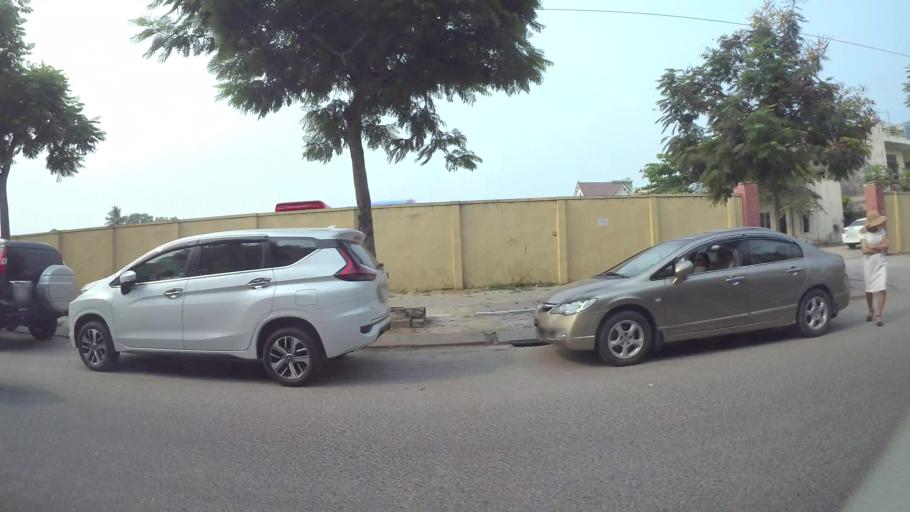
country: VN
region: Da Nang
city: Son Tra
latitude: 16.0448
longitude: 108.2161
